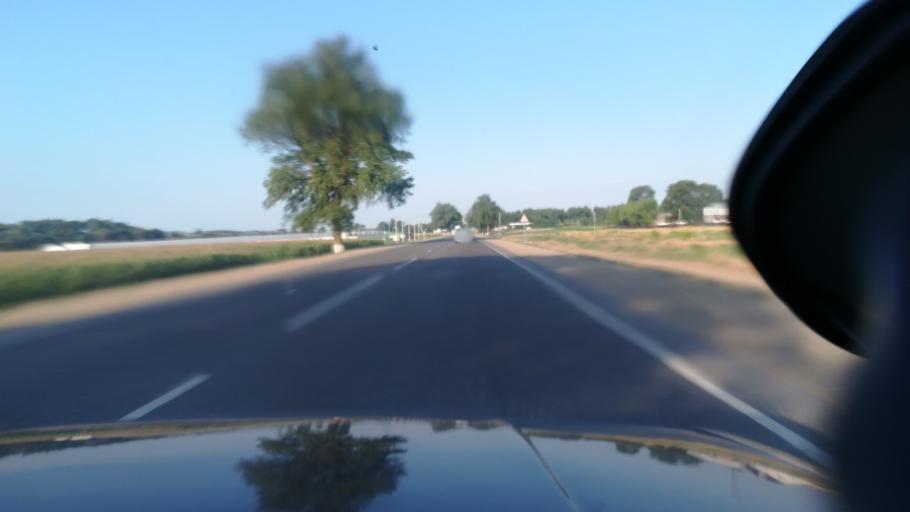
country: RU
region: Krasnodarskiy
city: Yurovka
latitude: 45.1188
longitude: 37.3939
